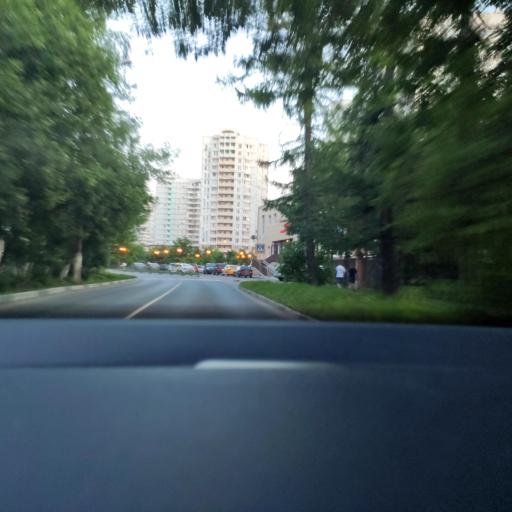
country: RU
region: Moskovskaya
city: Zheleznodorozhnyy
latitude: 55.7496
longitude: 37.9862
